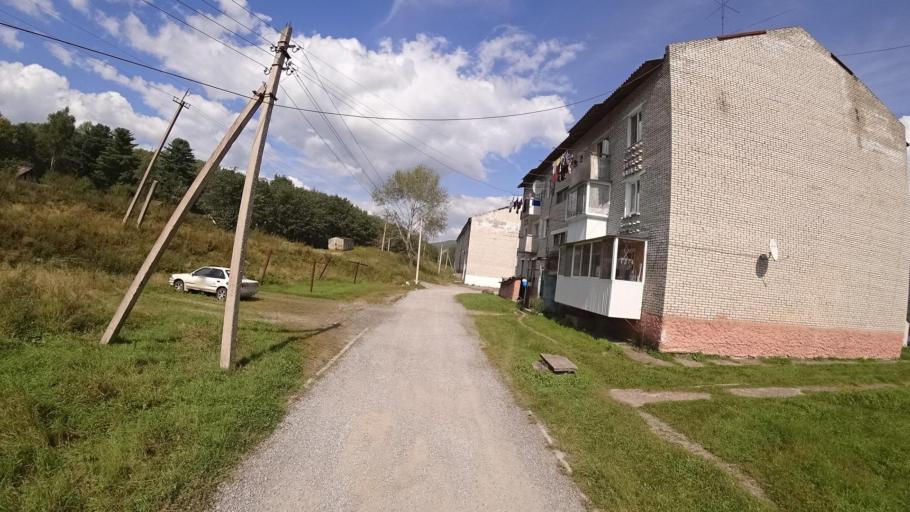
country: RU
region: Jewish Autonomous Oblast
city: Londoko
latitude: 49.0274
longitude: 131.9217
